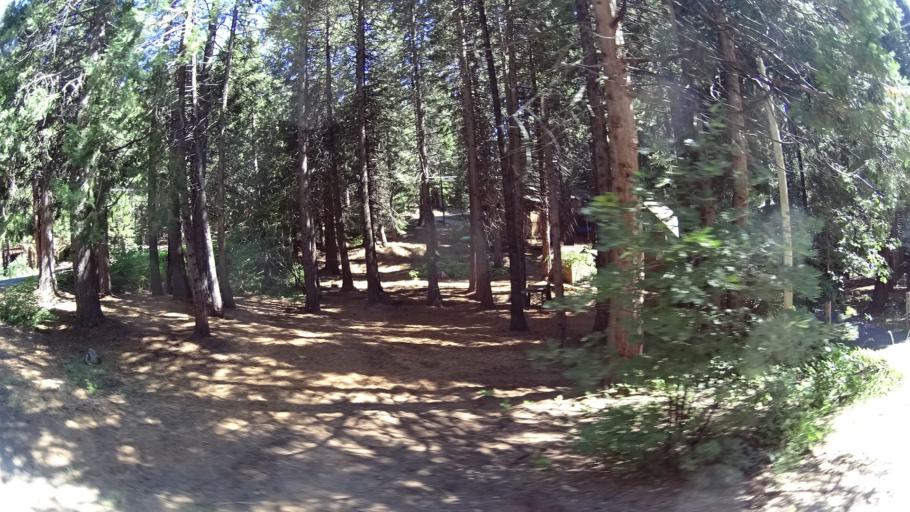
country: US
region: California
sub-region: Calaveras County
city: Arnold
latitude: 38.2856
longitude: -120.2782
